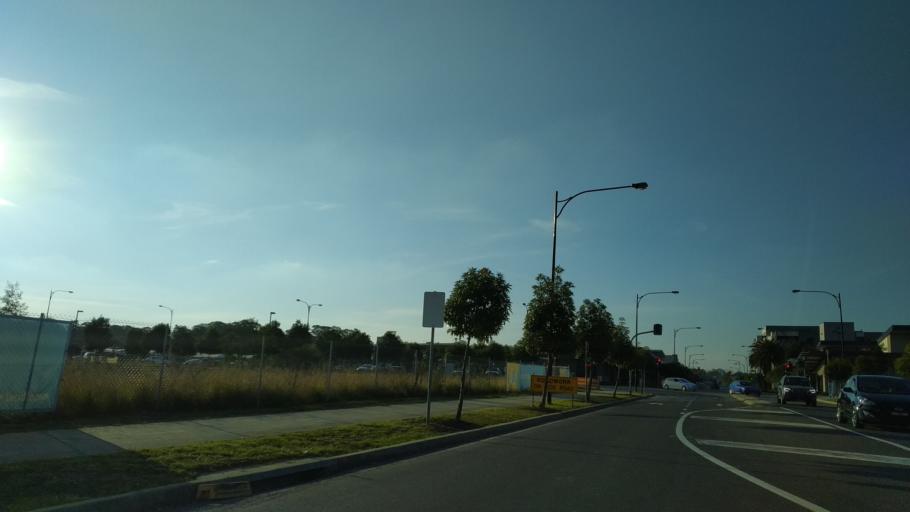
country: AU
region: New South Wales
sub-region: Penrith Municipality
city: Werrington Downs
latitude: -33.7287
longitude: 150.7258
